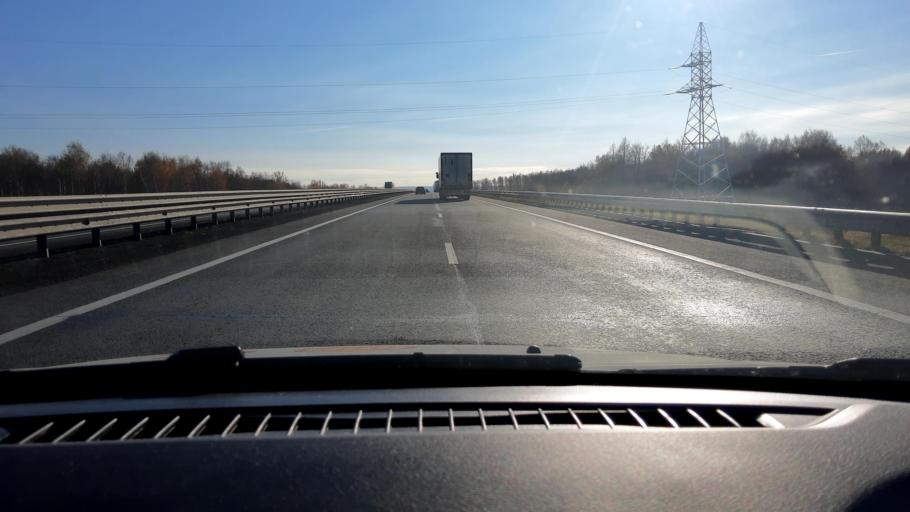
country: RU
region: Nizjnij Novgorod
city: Burevestnik
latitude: 56.1366
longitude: 43.7694
